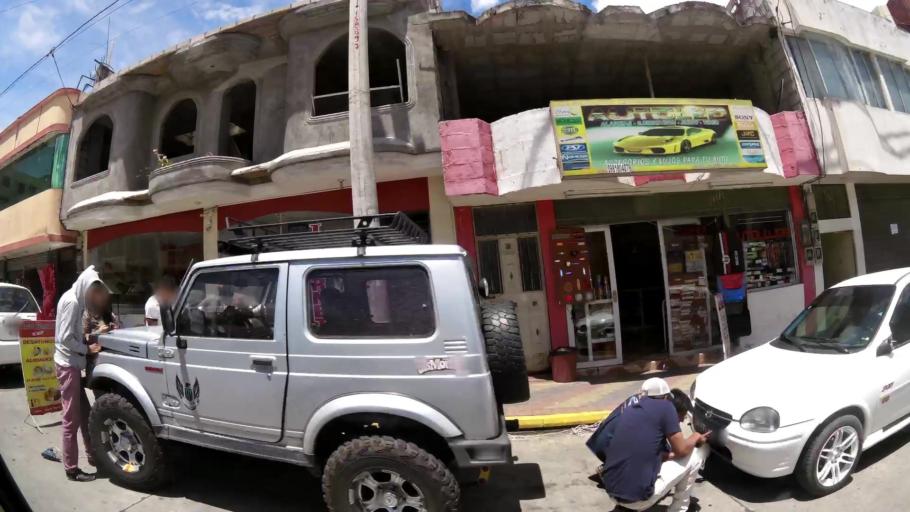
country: EC
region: Tungurahua
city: Pelileo
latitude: -1.3329
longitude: -78.5543
